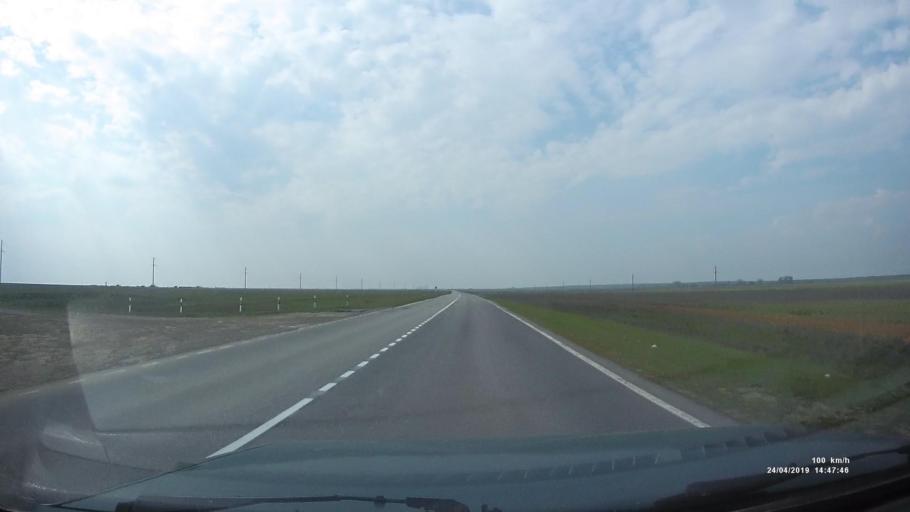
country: RU
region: Rostov
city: Remontnoye
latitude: 46.4943
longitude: 43.7677
